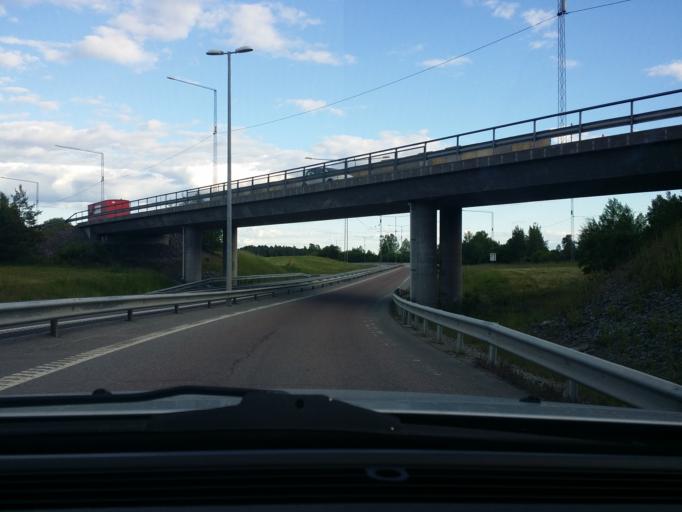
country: SE
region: Stockholm
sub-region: Sigtuna Kommun
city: Rosersberg
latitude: 59.6062
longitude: 17.8952
